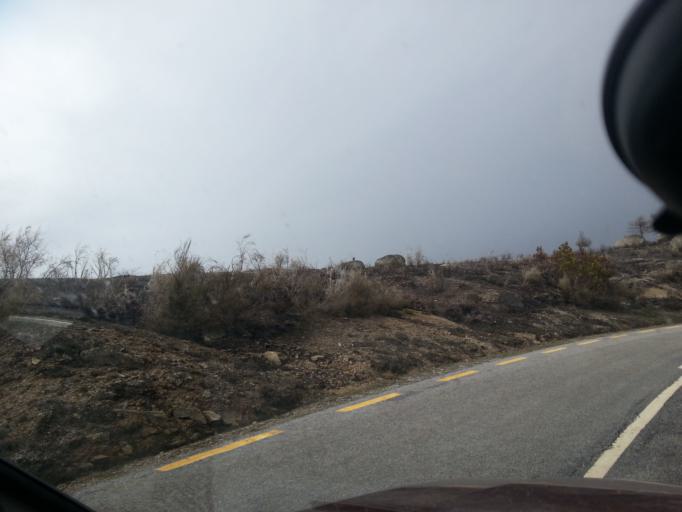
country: PT
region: Guarda
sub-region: Manteigas
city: Manteigas
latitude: 40.4207
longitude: -7.5929
